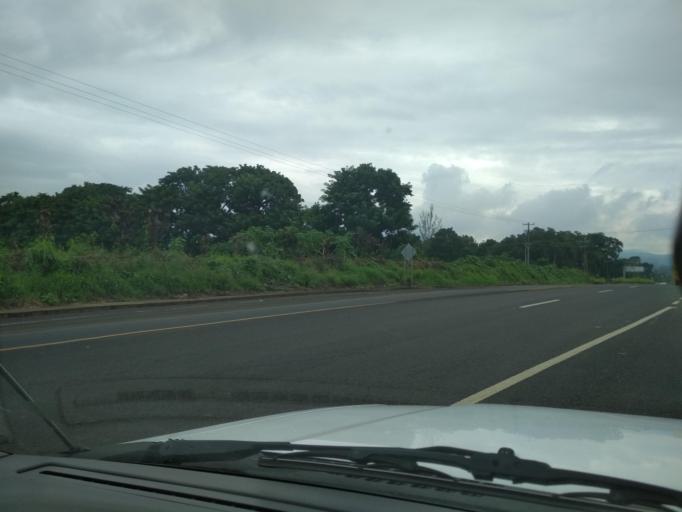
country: MX
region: Veracruz
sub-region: San Andres Tuxtla
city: Matacapan
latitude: 18.4354
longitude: -95.1726
